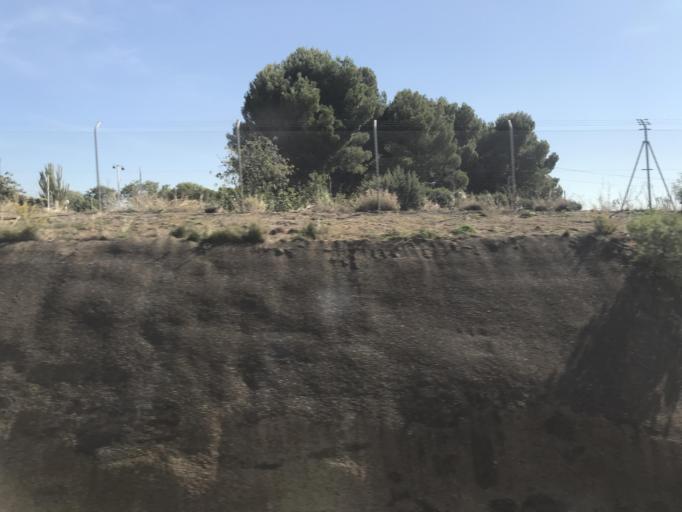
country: ES
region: Aragon
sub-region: Provincia de Zaragoza
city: Oliver-Valdefierro, Oliver, Valdefierro
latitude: 41.6639
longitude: -0.9450
